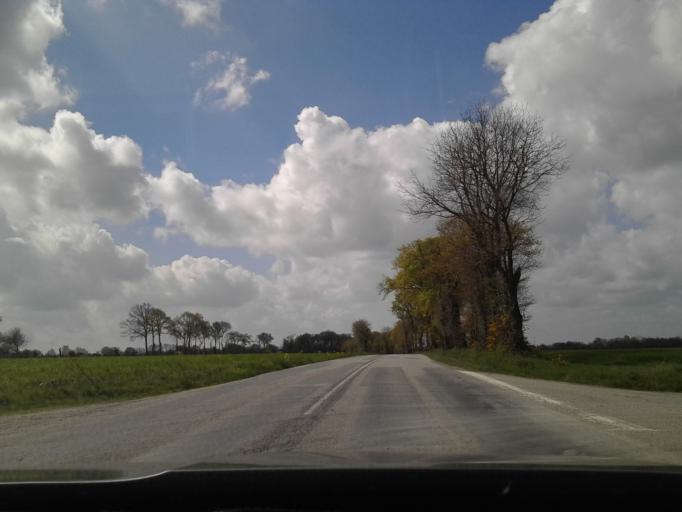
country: FR
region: Brittany
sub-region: Departement d'Ille-et-Vilaine
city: Grand-Fougeray
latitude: 47.7370
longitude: -1.7204
